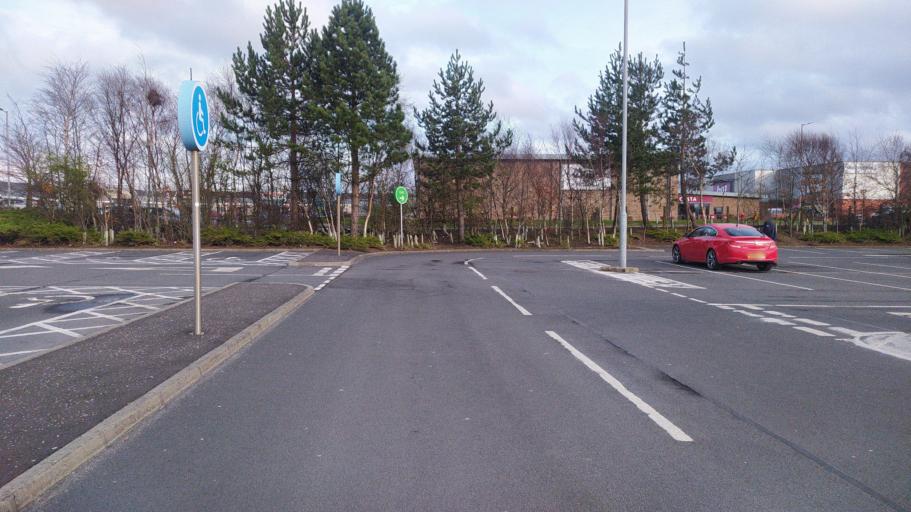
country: GB
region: Scotland
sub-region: South Ayrshire
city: Prestwick
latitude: 55.4797
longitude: -4.5963
